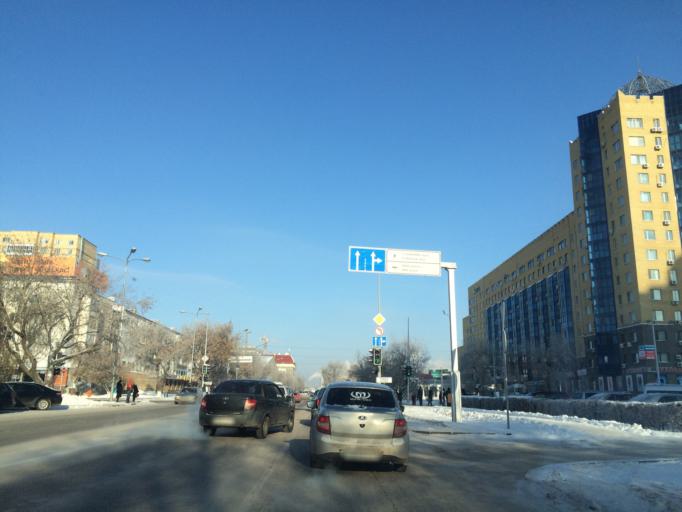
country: KZ
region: Astana Qalasy
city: Astana
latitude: 51.1693
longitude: 71.4394
